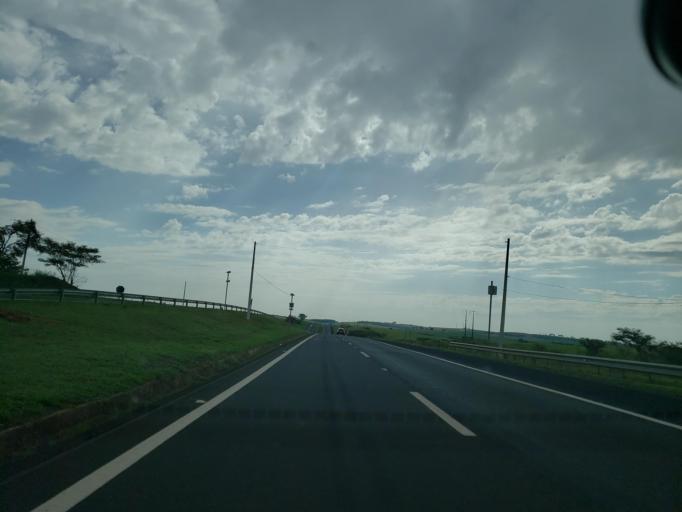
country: BR
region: Sao Paulo
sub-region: Cafelandia
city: Cafelandia
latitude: -21.7558
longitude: -49.6797
